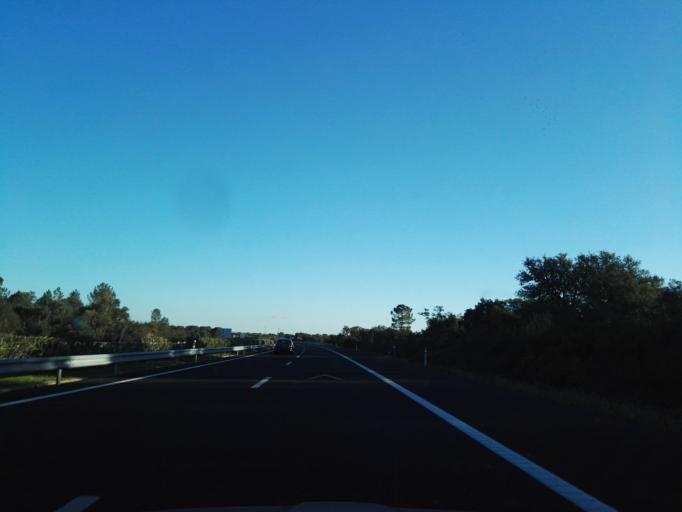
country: PT
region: Santarem
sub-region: Benavente
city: Poceirao
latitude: 38.8737
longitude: -8.7920
